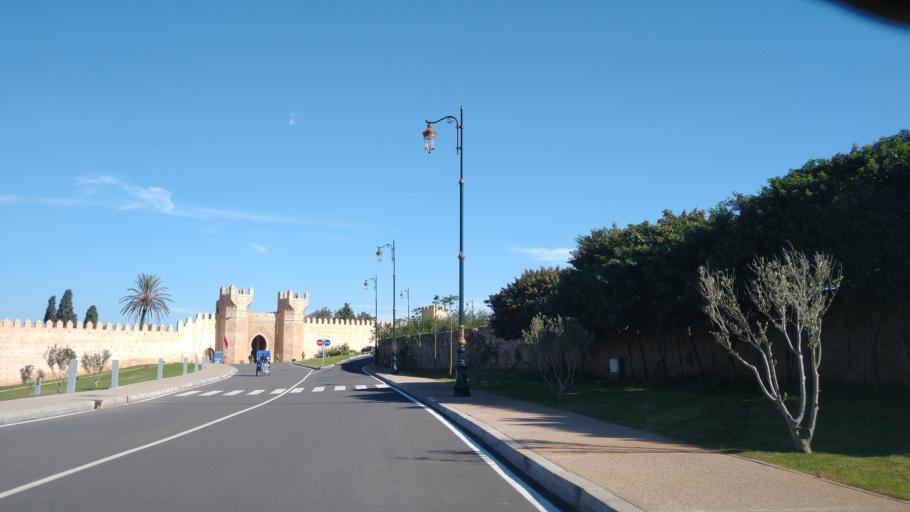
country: MA
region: Rabat-Sale-Zemmour-Zaer
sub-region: Rabat
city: Rabat
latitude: 34.0063
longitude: -6.8247
